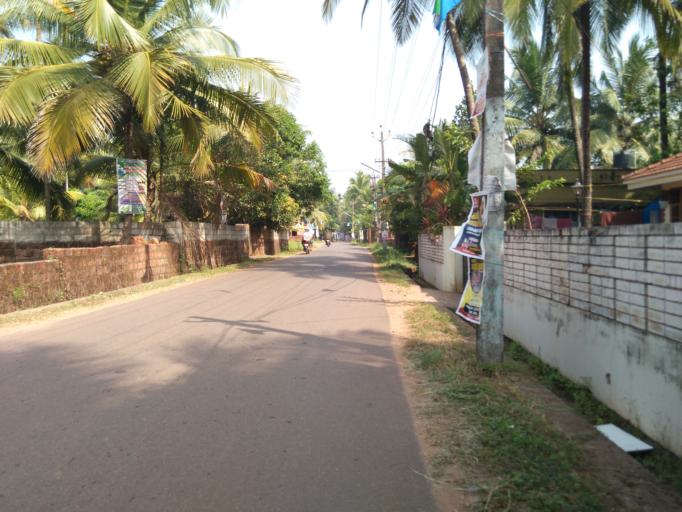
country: IN
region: Kerala
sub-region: Kozhikode
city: Kunnamangalam
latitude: 11.2895
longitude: 75.8360
